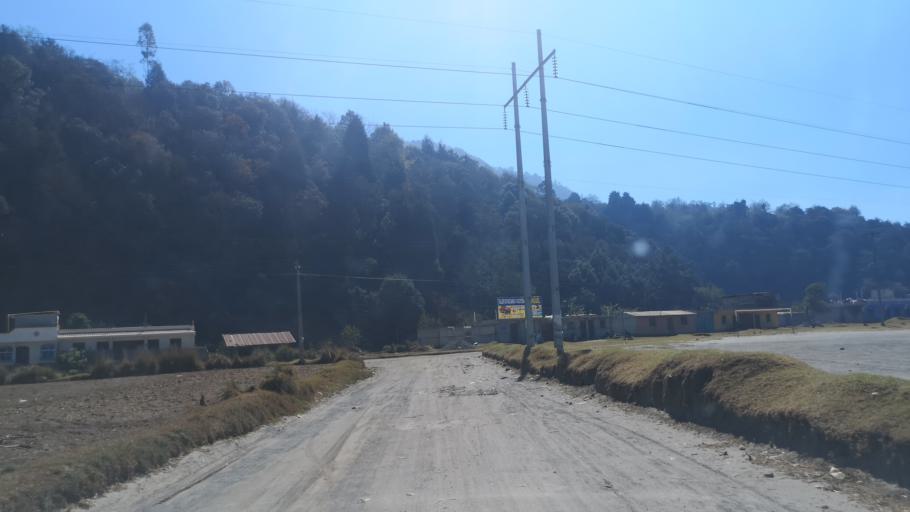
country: GT
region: Quetzaltenango
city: Almolonga
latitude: 14.7883
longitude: -91.5375
